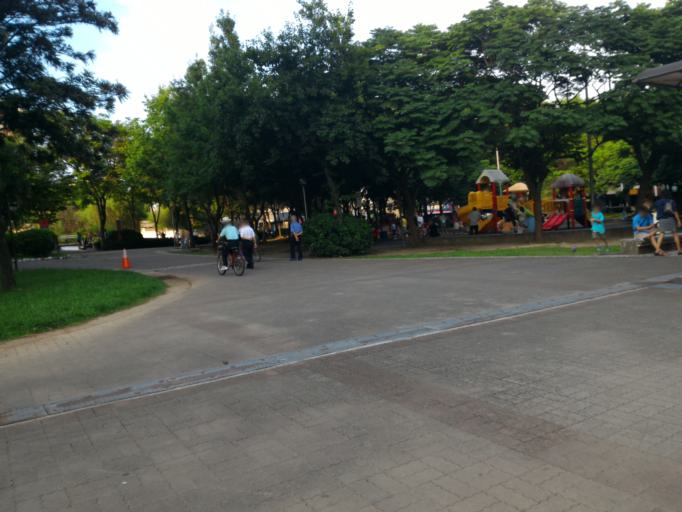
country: TW
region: Taipei
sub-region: Taipei
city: Banqiao
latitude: 25.0014
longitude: 121.5140
